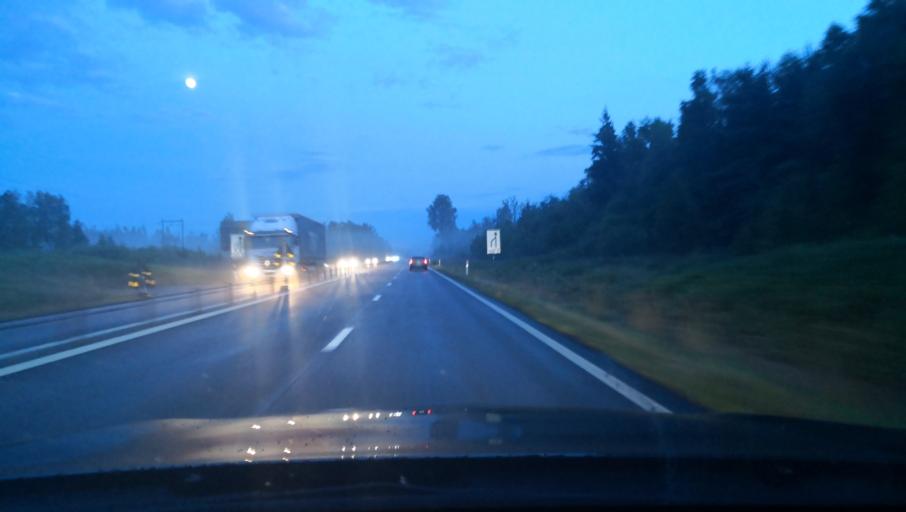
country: SE
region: Kronoberg
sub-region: Almhults Kommun
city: AElmhult
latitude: 56.5290
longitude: 14.1422
